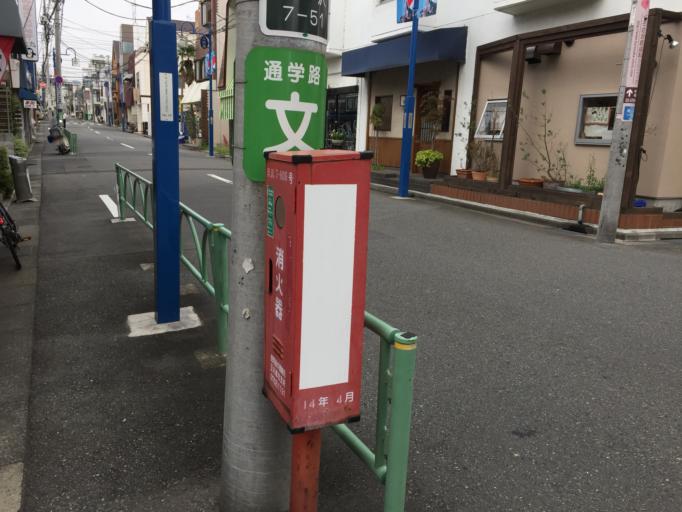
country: JP
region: Tokyo
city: Tokyo
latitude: 35.6091
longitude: 139.6628
